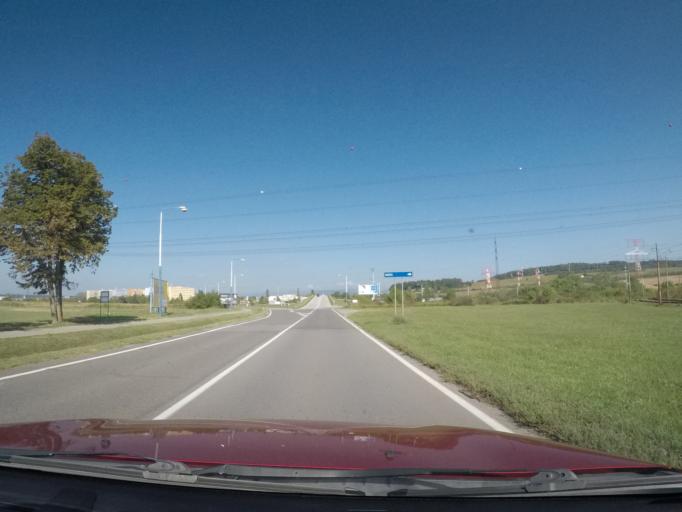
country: SK
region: Kosicky
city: Kosice
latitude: 48.6268
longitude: 21.1858
